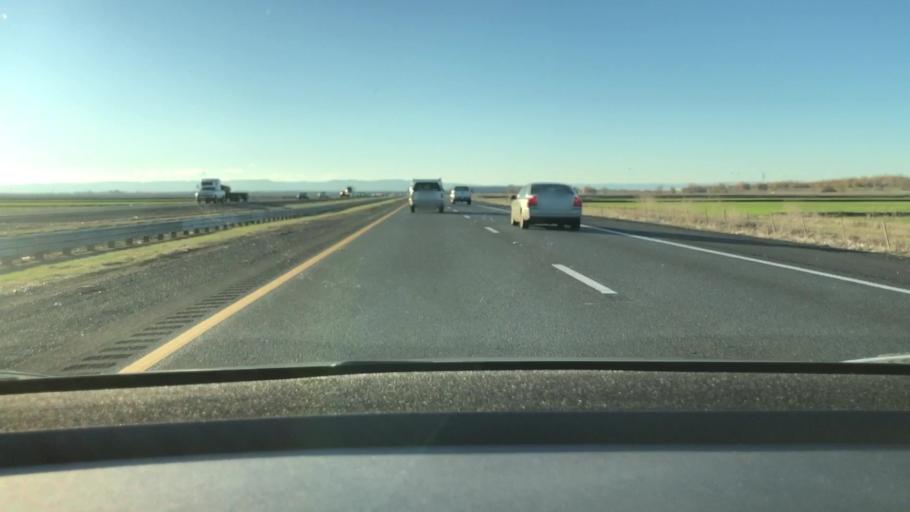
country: US
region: California
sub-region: Yolo County
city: Woodland
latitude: 38.6741
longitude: -121.6893
